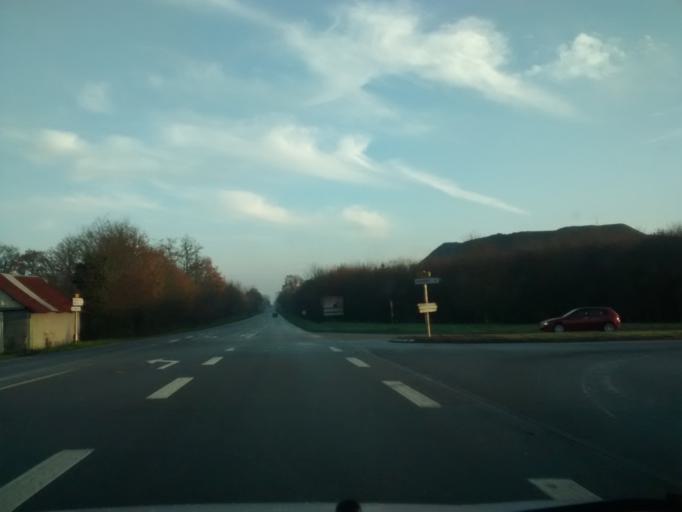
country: FR
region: Brittany
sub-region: Departement d'Ille-et-Vilaine
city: Sens-de-Bretagne
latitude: 48.3112
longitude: -1.5391
